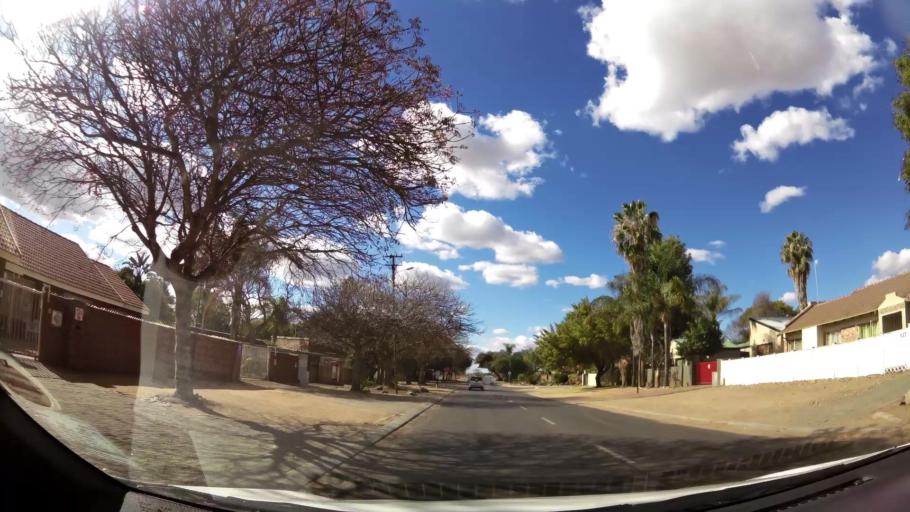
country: ZA
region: Limpopo
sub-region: Capricorn District Municipality
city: Polokwane
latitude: -23.8816
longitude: 29.4699
